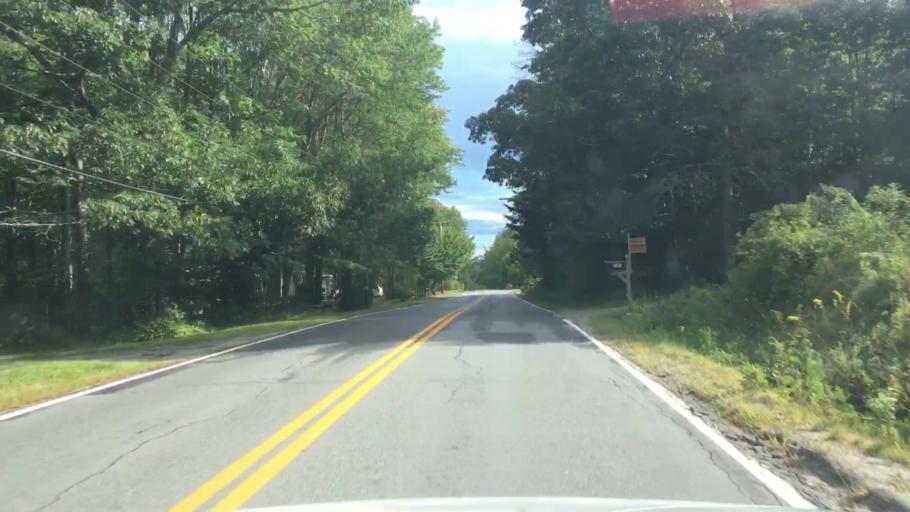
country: US
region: Maine
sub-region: Hancock County
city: Trenton
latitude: 44.4308
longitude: -68.3973
